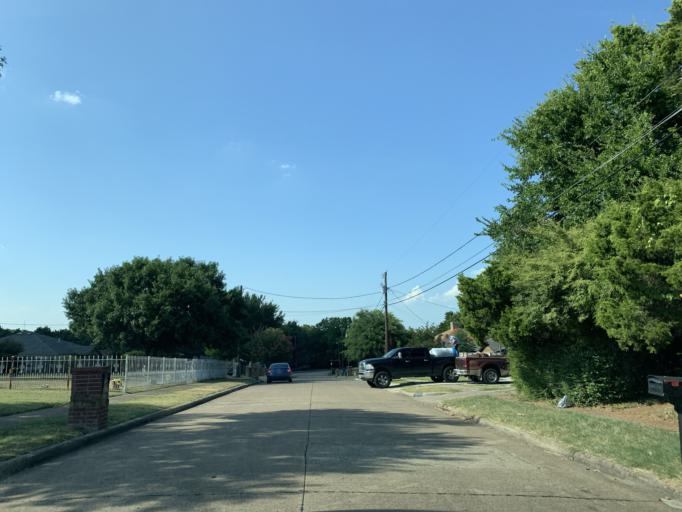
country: US
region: Texas
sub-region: Dallas County
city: Hutchins
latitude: 32.6573
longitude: -96.7781
